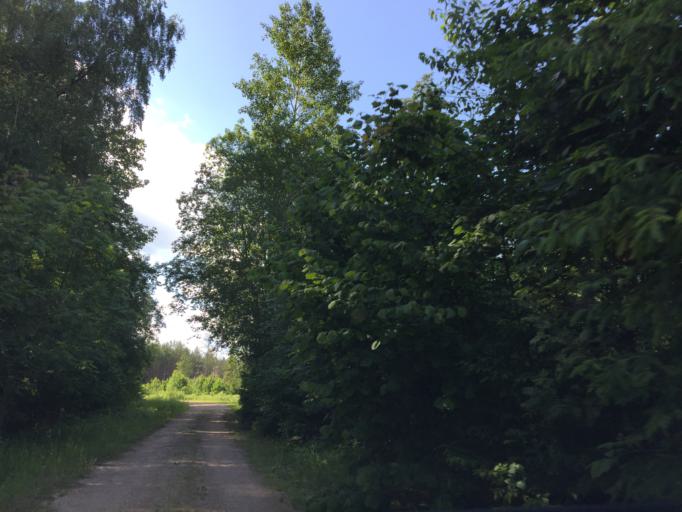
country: LV
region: Tukuma Rajons
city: Tukums
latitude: 57.0223
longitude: 23.2366
